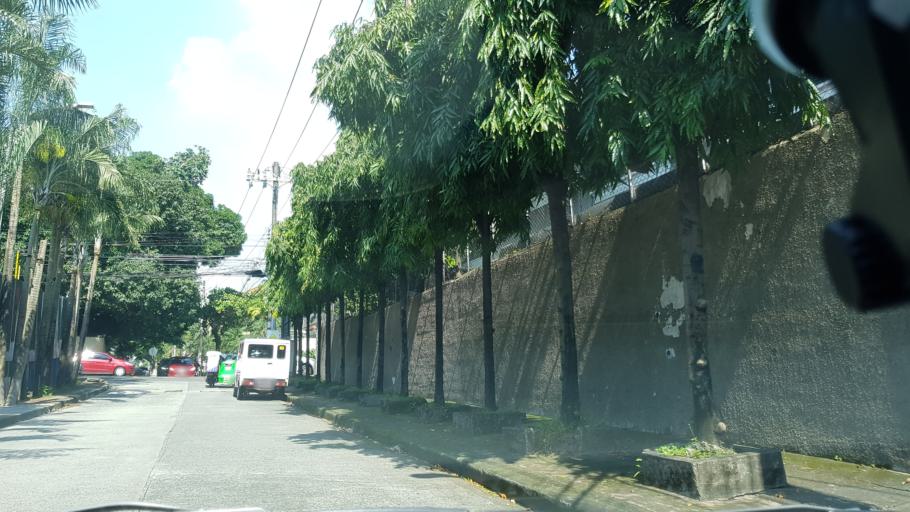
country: PH
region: Metro Manila
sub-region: San Juan
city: San Juan
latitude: 14.6151
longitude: 121.0334
